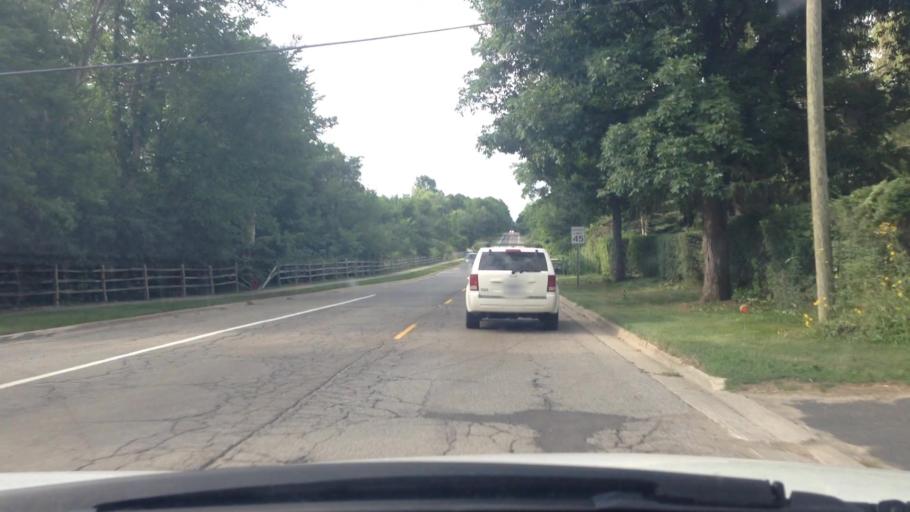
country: US
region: Michigan
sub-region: Oakland County
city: Clarkston
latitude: 42.7503
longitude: -83.3507
